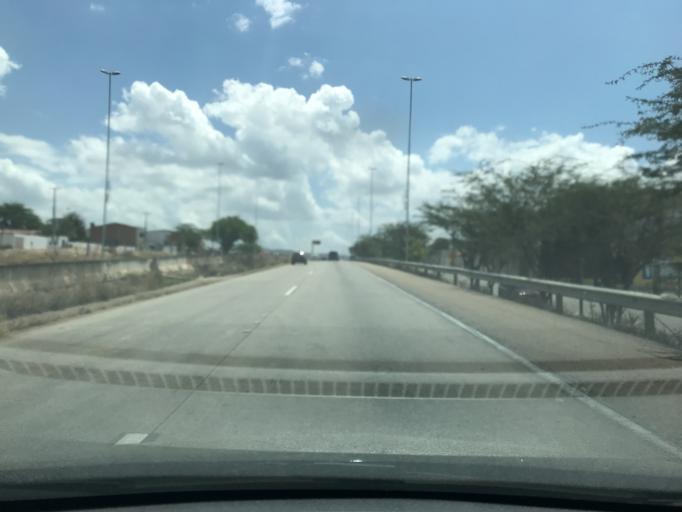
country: BR
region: Pernambuco
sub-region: Bezerros
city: Bezerros
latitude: -8.2995
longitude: -35.8421
